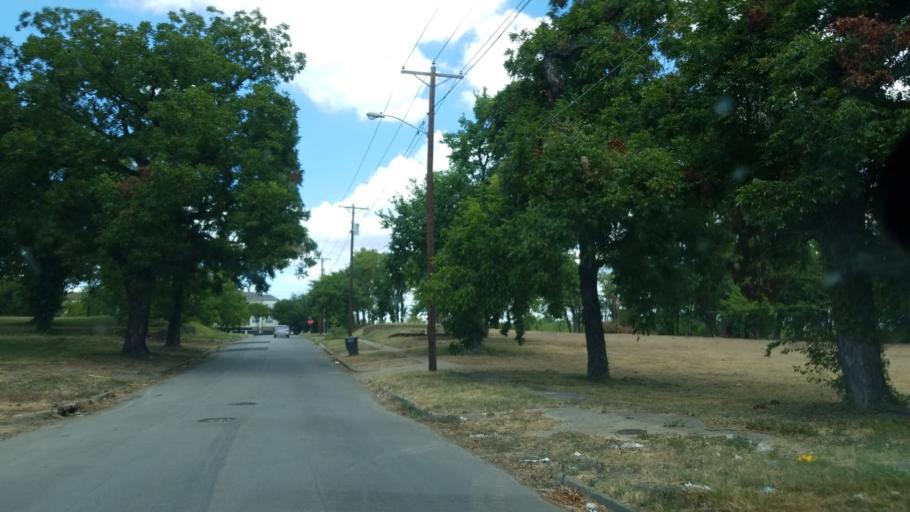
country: US
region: Texas
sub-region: Dallas County
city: Dallas
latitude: 32.7611
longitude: -96.8216
